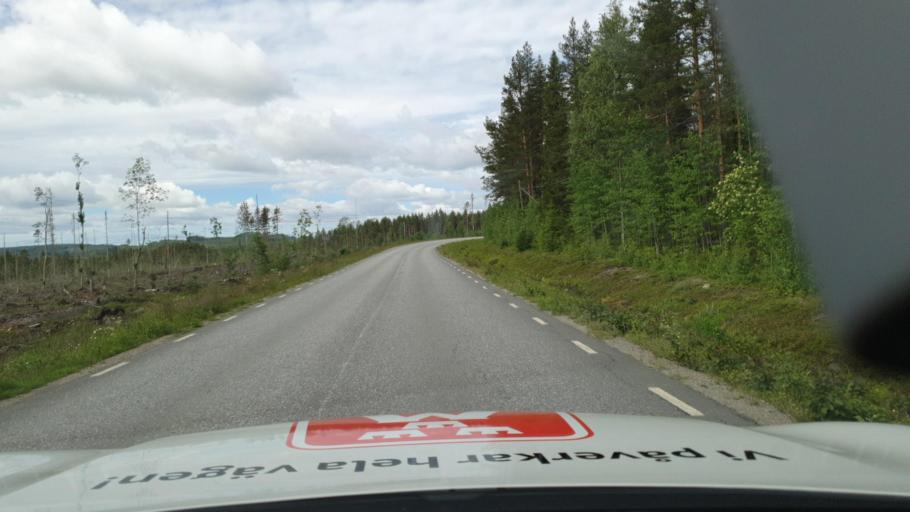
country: SE
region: Vaesterbotten
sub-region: Dorotea Kommun
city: Dorotea
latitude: 64.2674
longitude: 16.3503
